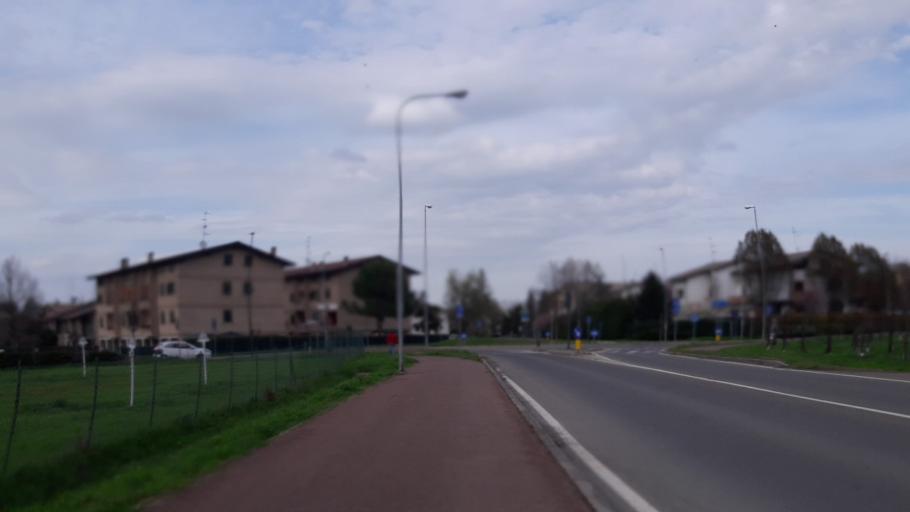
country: IT
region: Emilia-Romagna
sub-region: Provincia di Reggio Emilia
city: Reggio nell'Emilia
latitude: 44.6842
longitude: 10.6008
